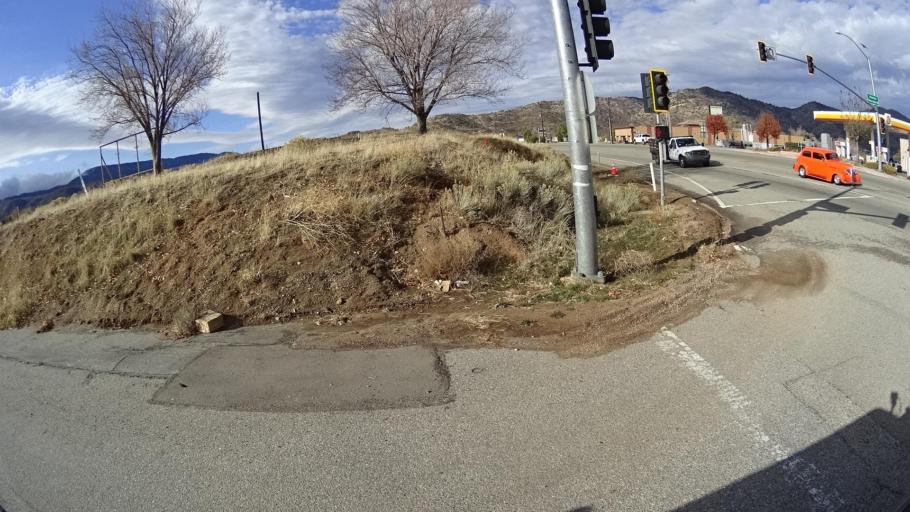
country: US
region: California
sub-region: Kern County
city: Golden Hills
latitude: 35.1242
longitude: -118.4949
